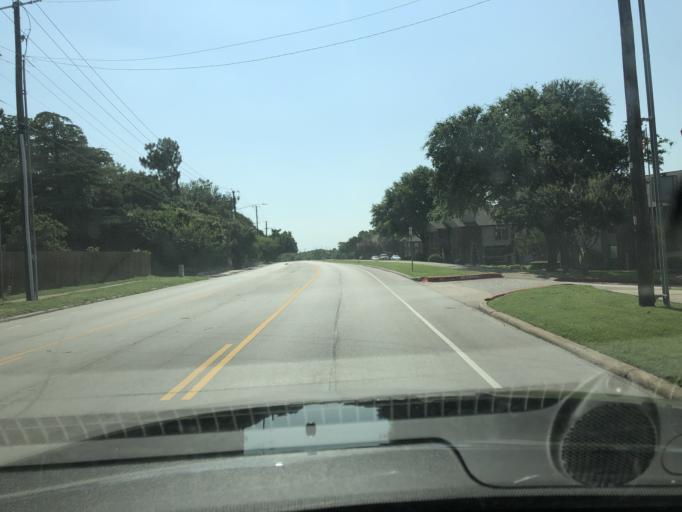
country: US
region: Texas
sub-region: Dallas County
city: Sunnyvale
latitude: 32.8356
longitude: -96.5868
